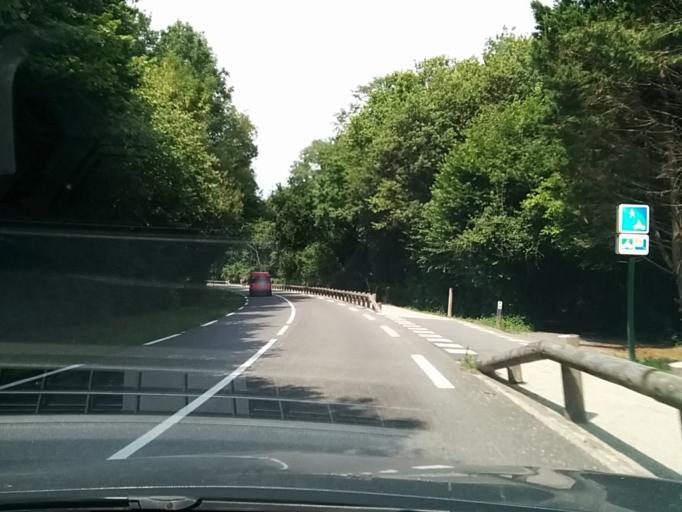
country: FR
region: Aquitaine
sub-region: Departement des Pyrenees-Atlantiques
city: Hendaye
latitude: 43.3775
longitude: -1.7452
